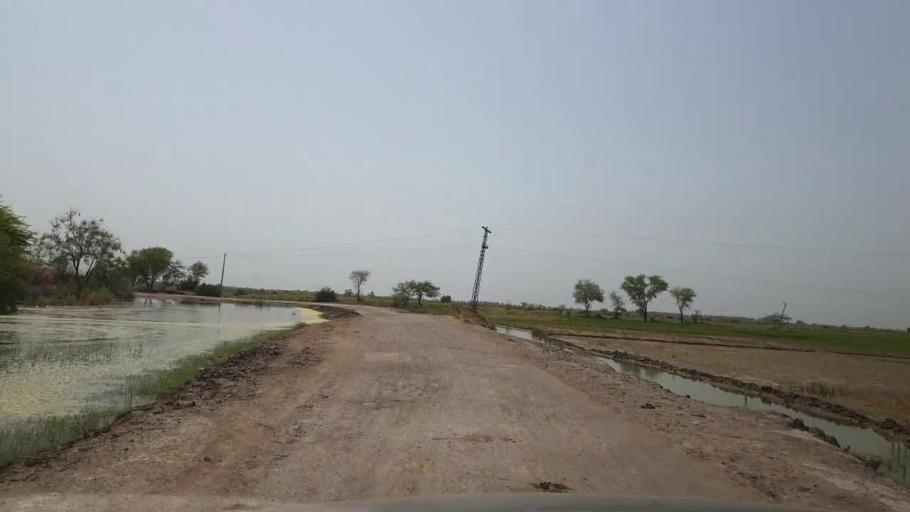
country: PK
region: Sindh
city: Garhi Yasin
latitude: 27.8951
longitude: 68.4720
